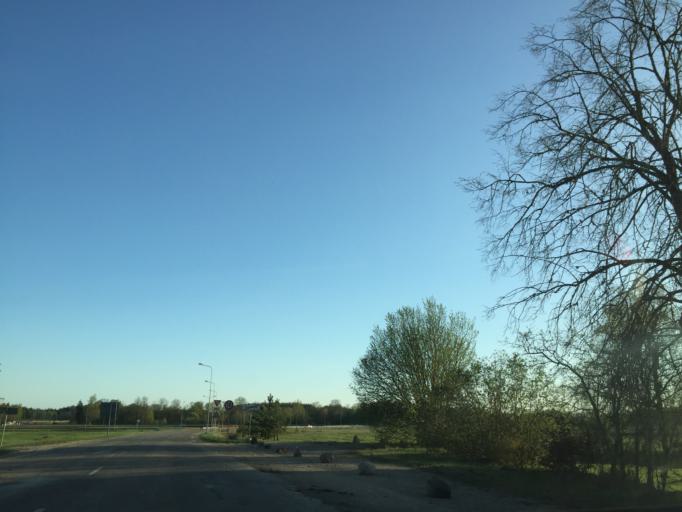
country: LV
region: Koknese
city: Koknese
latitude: 56.6687
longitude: 25.4676
